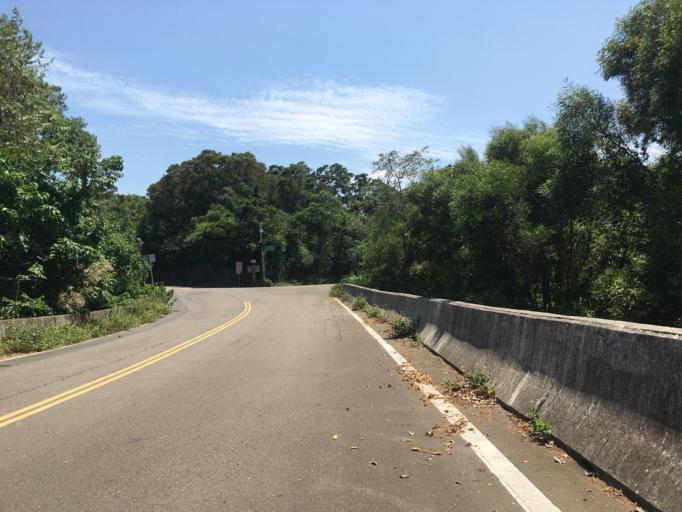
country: TW
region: Taiwan
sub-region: Hsinchu
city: Hsinchu
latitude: 24.7337
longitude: 120.9873
